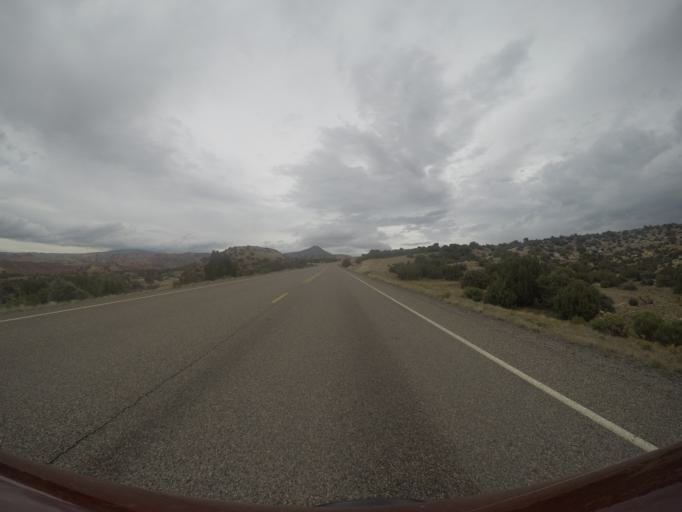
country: US
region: Wyoming
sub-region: Big Horn County
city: Lovell
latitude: 44.9851
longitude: -108.2610
